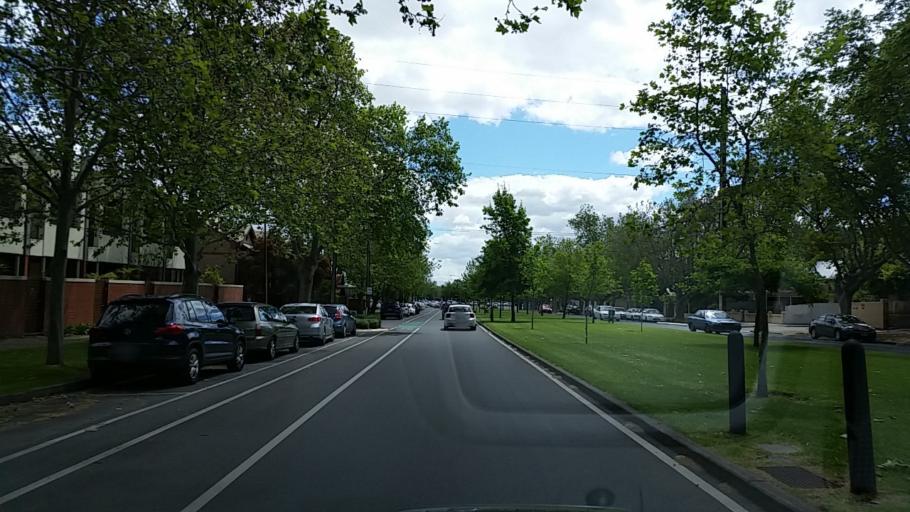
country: AU
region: South Australia
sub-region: Norwood Payneham St Peters
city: Trinity Gardens
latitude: -34.9178
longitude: 138.6318
